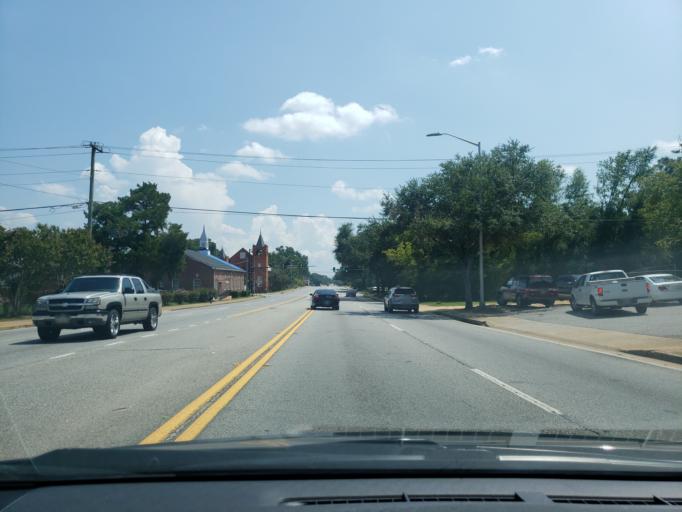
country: US
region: Georgia
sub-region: Dougherty County
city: Albany
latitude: 31.5734
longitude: -84.1560
